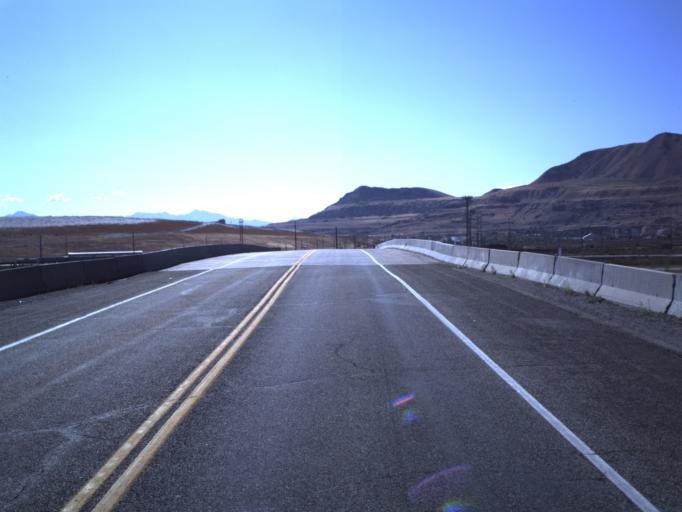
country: US
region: Utah
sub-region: Salt Lake County
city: Magna
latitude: 40.7457
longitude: -112.1838
